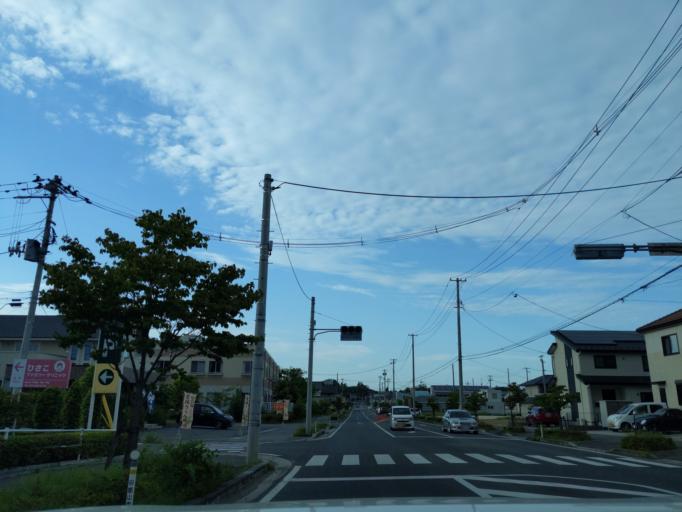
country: JP
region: Fukushima
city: Koriyama
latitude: 37.4195
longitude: 140.3348
